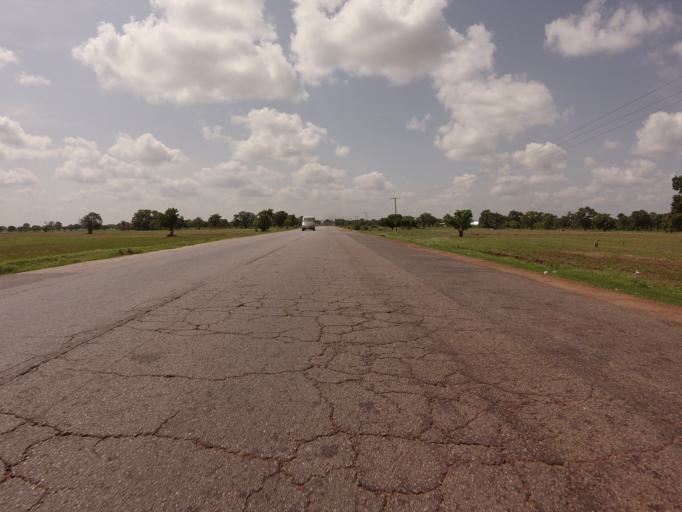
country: GH
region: Northern
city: Savelugu
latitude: 9.5581
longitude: -0.8367
